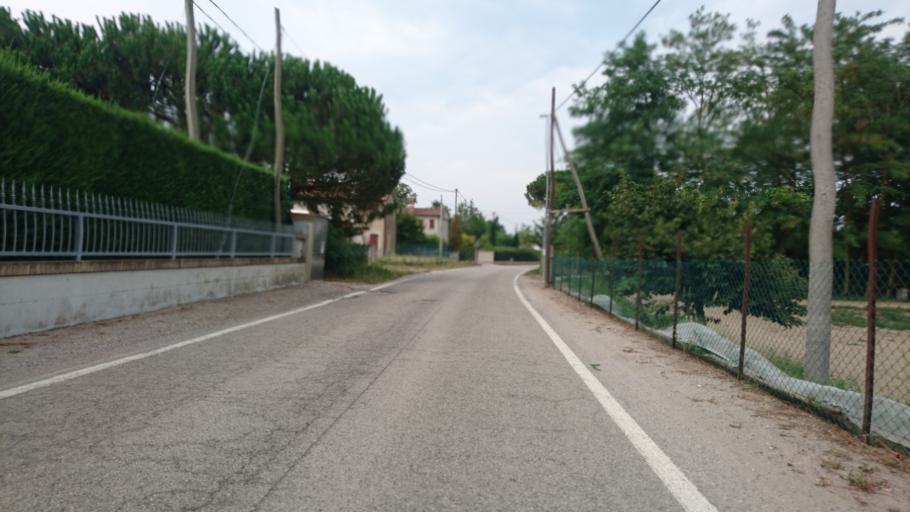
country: IT
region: Veneto
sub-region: Provincia di Rovigo
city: Rosolina
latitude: 45.0783
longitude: 12.2297
